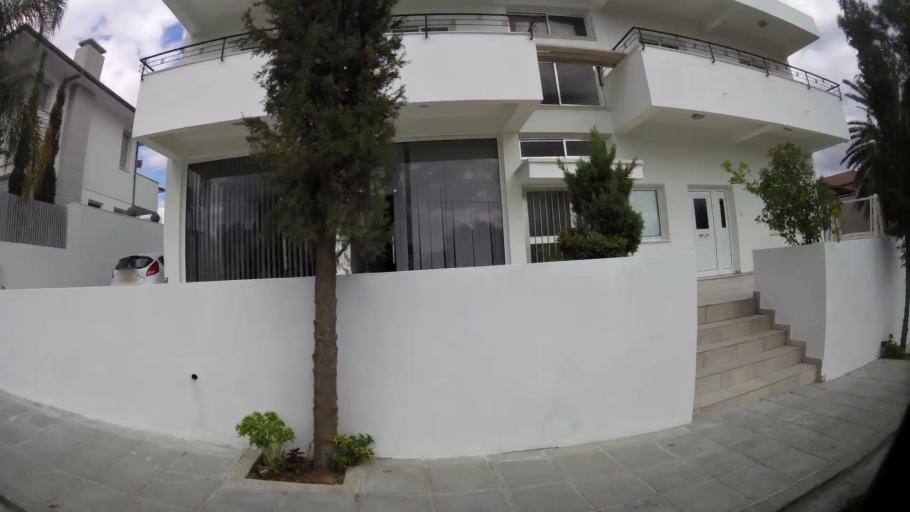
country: CY
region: Lefkosia
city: Nicosia
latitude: 35.1776
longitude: 33.3884
